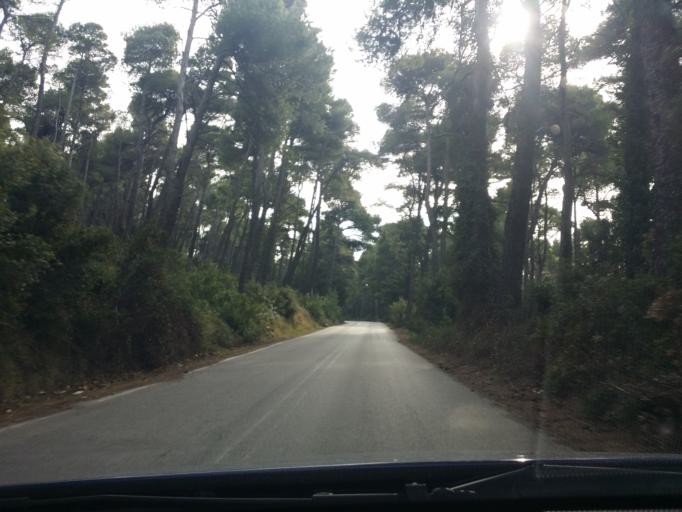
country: GR
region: Attica
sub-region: Nomarchia Anatolikis Attikis
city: Varybobi
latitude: 38.1539
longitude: 23.7917
